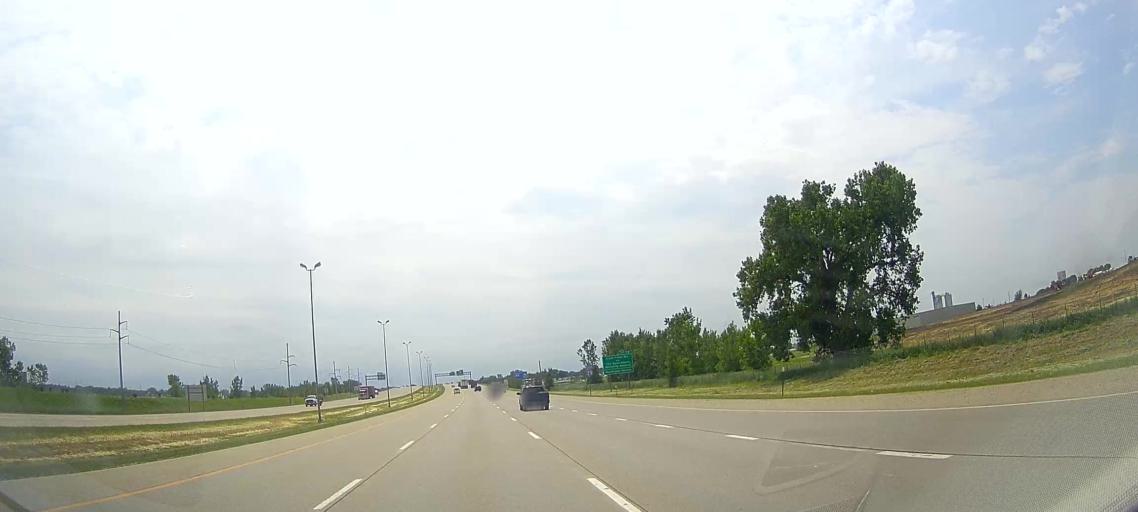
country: US
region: South Dakota
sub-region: Minnehaha County
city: Sioux Falls
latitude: 43.5529
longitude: -96.7805
